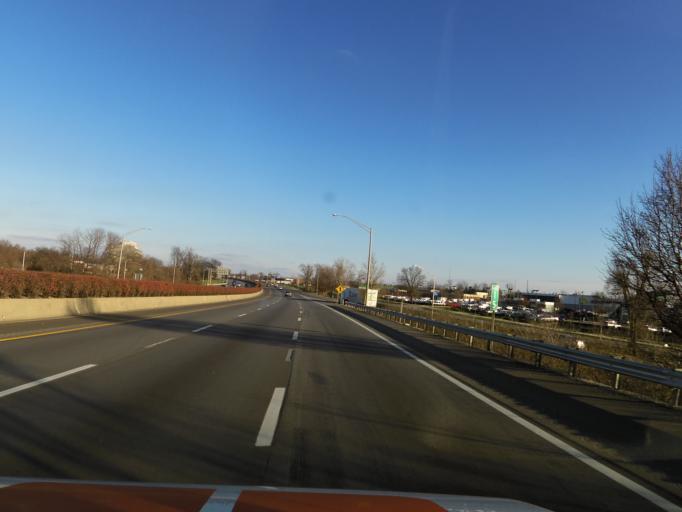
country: US
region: Kentucky
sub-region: Jefferson County
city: Hurstbourne Acres
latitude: 38.2230
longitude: -85.5771
